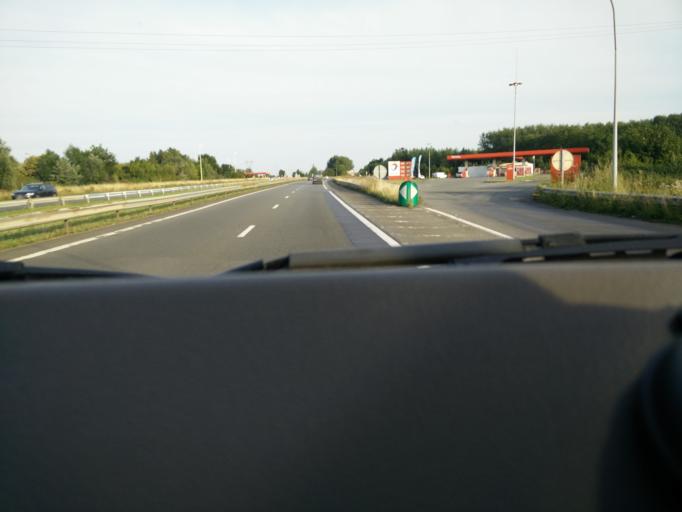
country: FR
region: Nord-Pas-de-Calais
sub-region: Departement du Nord
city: Genech
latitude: 50.5201
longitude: 3.2041
